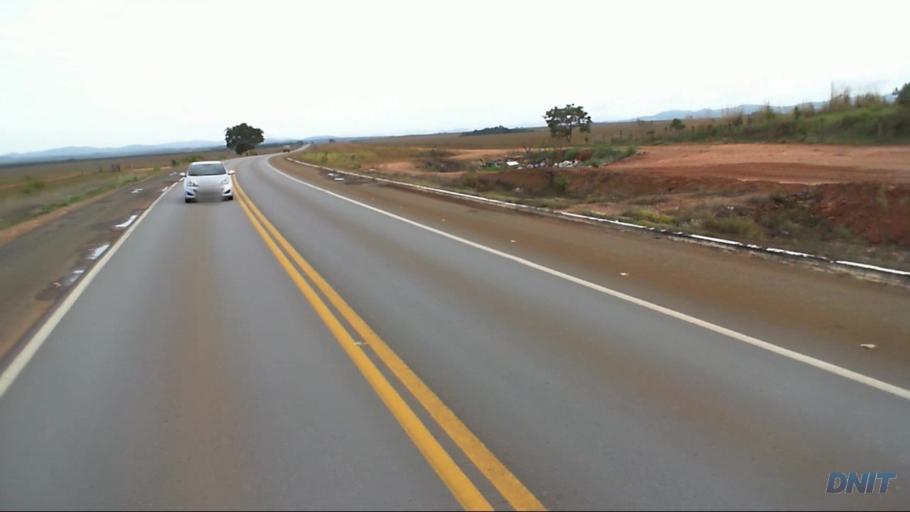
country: BR
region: Goias
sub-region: Uruacu
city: Uruacu
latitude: -14.6530
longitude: -49.1610
